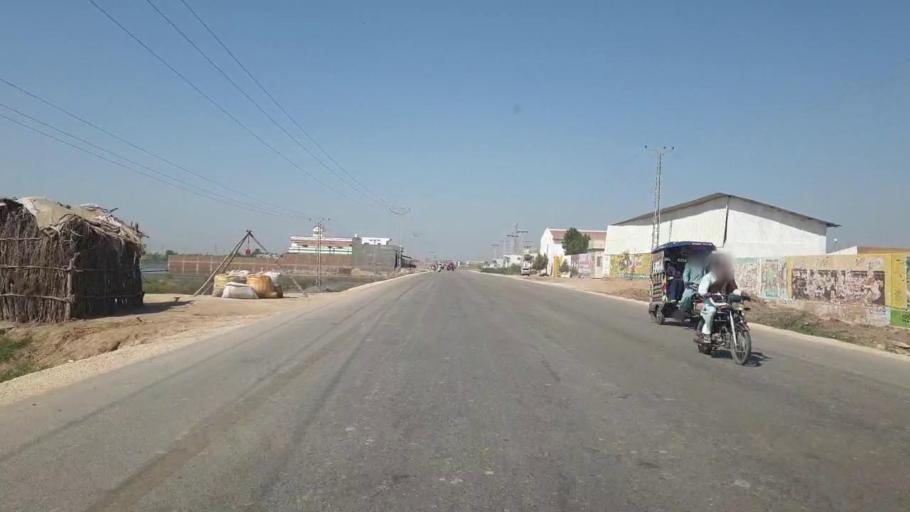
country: PK
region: Sindh
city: Talhar
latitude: 24.8767
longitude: 68.8142
